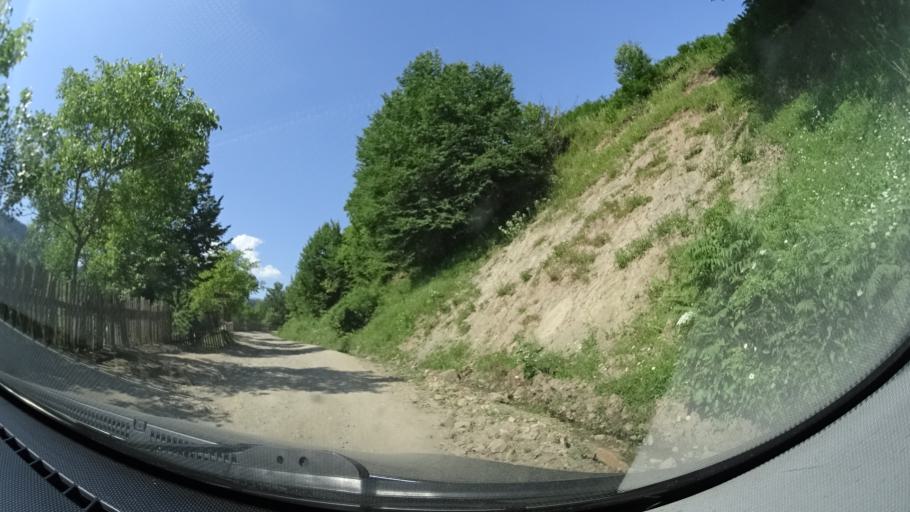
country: GE
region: Ajaria
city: Dioknisi
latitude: 41.6486
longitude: 42.4586
